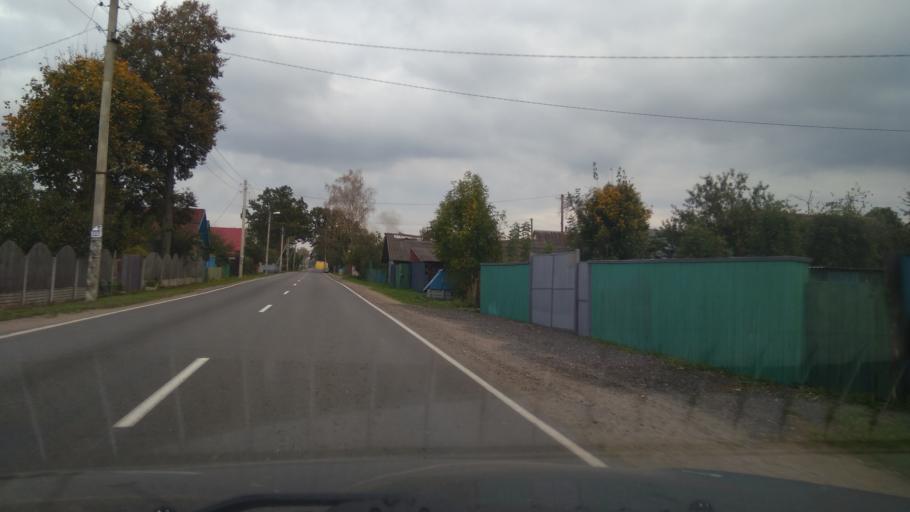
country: BY
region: Minsk
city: Dukora
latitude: 53.6700
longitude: 27.9413
